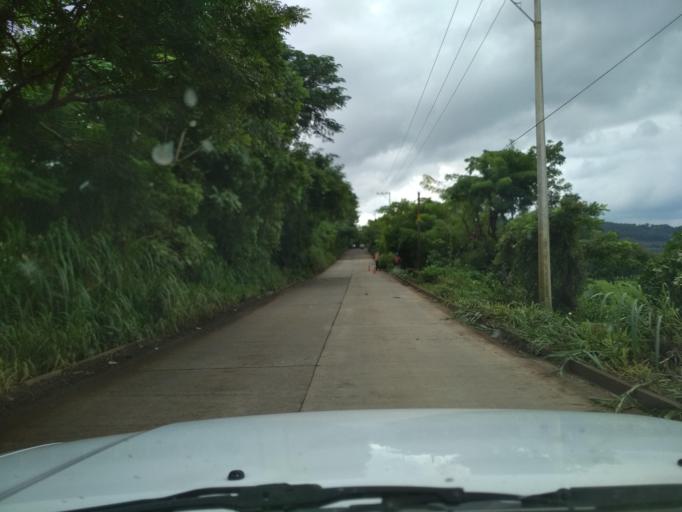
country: MX
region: Veracruz
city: Comoapan
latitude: 18.4178
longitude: -95.1774
